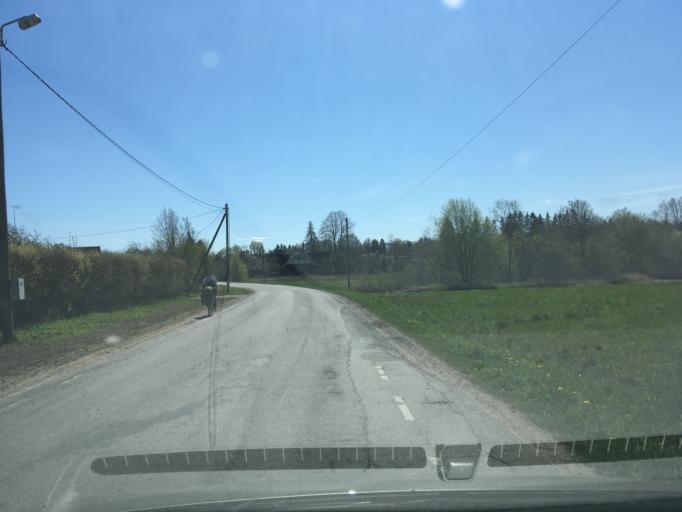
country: EE
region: Harju
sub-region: Raasiku vald
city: Arukula
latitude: 59.3747
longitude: 25.0774
